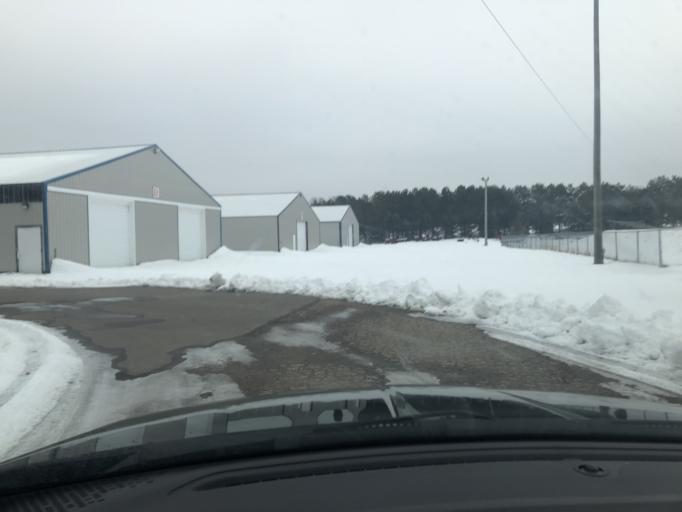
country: US
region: Minnesota
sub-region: Washington County
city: Lake Elmo
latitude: 45.0088
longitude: -92.8576
